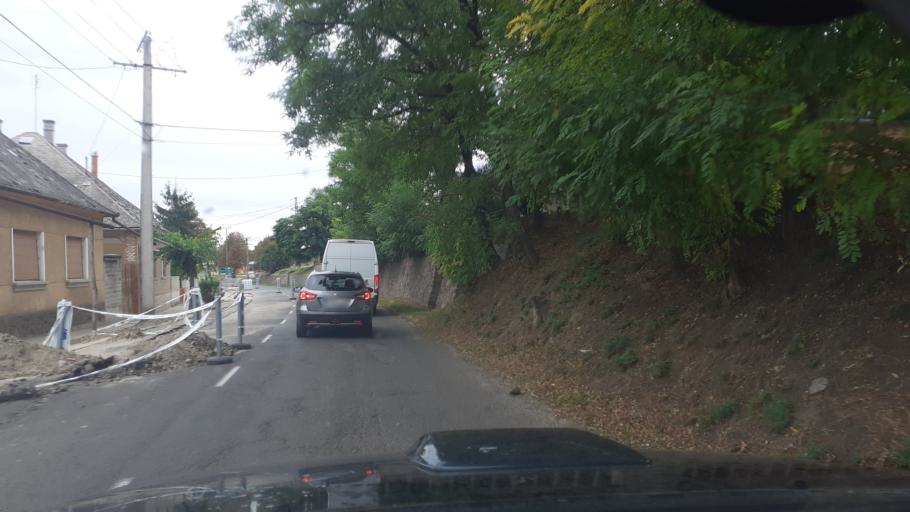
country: HU
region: Tolna
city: Dunafoldvar
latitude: 46.8032
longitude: 18.9304
